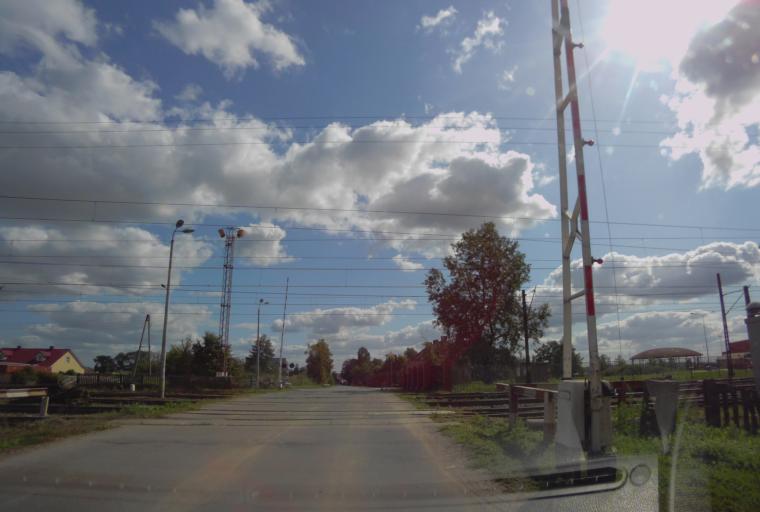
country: PL
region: Subcarpathian Voivodeship
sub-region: Tarnobrzeg
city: Tarnobrzeg
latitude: 50.5135
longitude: 21.6564
